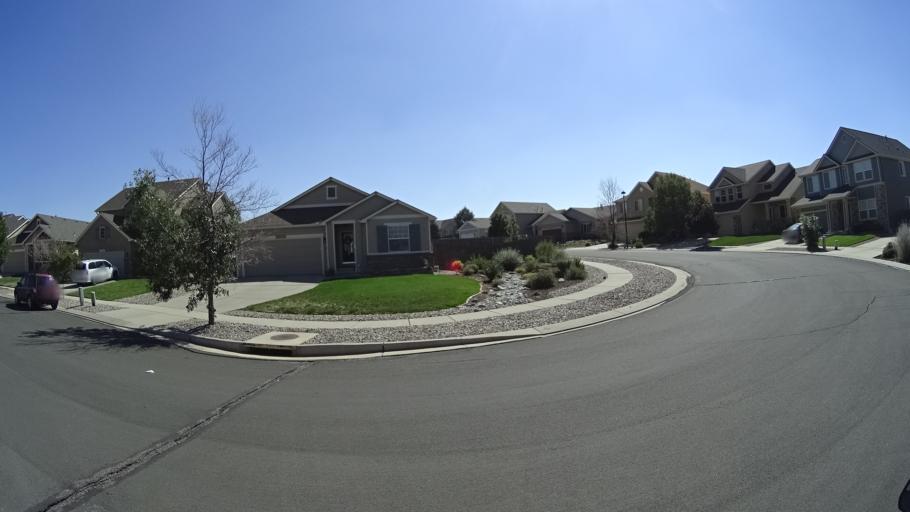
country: US
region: Colorado
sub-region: El Paso County
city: Cimarron Hills
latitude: 38.8968
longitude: -104.6977
